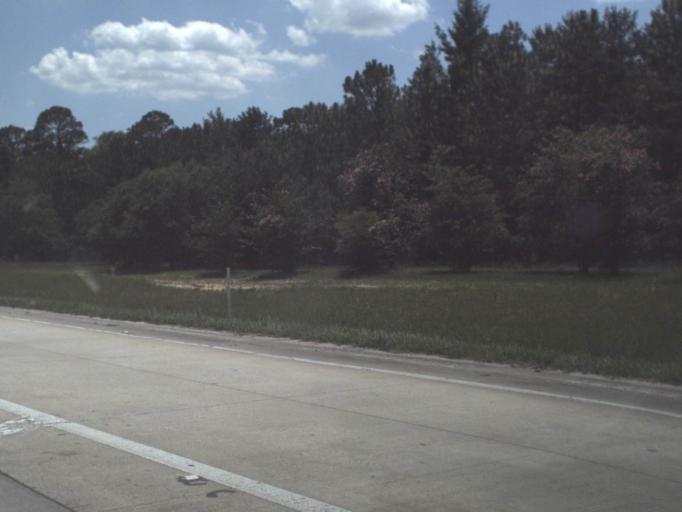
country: US
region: Florida
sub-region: Saint Johns County
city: Palm Valley
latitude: 30.2110
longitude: -81.5141
